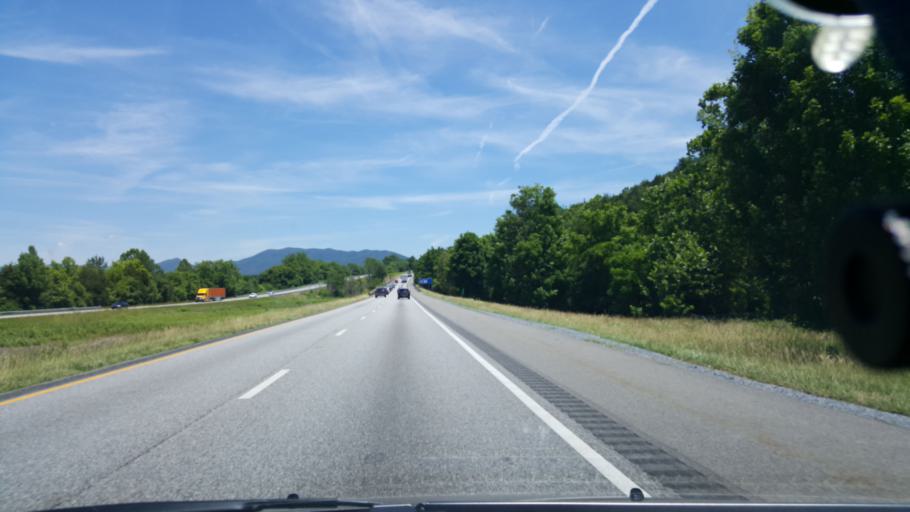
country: US
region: Virginia
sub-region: Botetourt County
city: Buchanan
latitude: 37.4885
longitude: -79.7700
